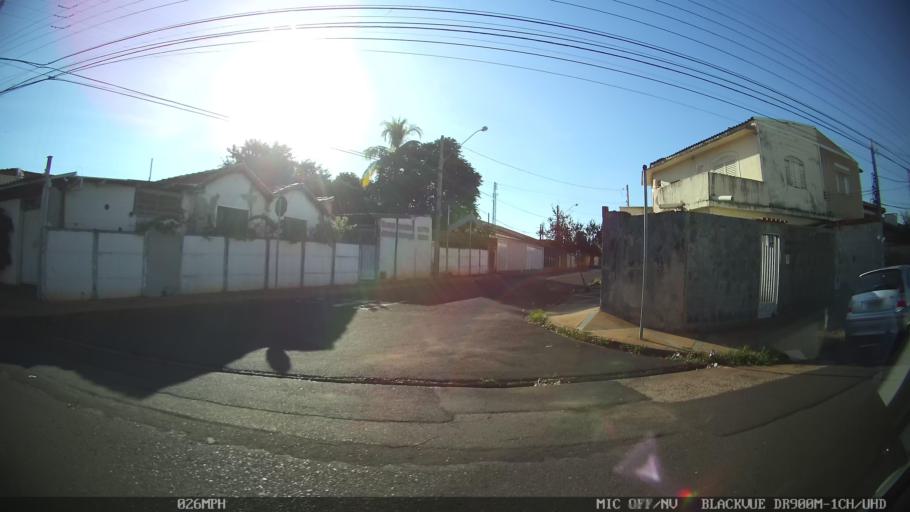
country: BR
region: Sao Paulo
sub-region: Sao Jose Do Rio Preto
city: Sao Jose do Rio Preto
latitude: -20.8112
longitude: -49.3966
